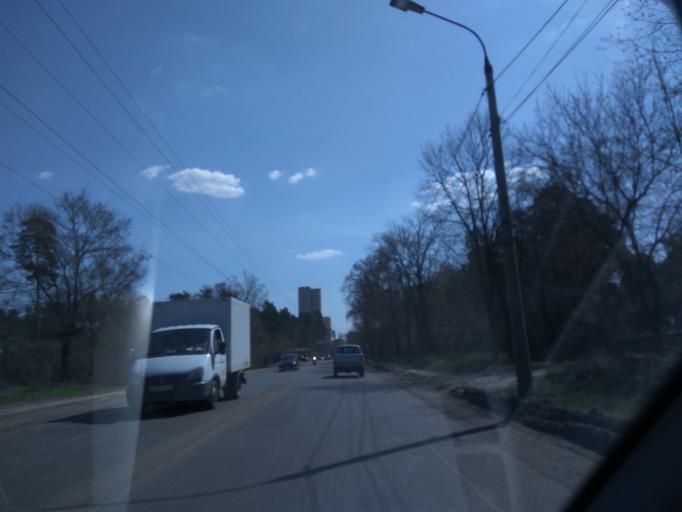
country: RU
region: Moskovskaya
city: Kratovo
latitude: 55.5702
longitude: 38.1895
